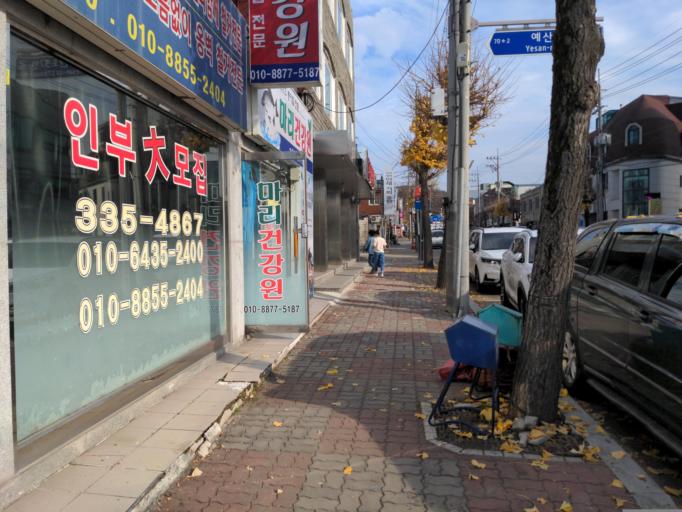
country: KR
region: Chungcheongnam-do
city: Yesan
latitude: 36.6822
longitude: 126.8303
